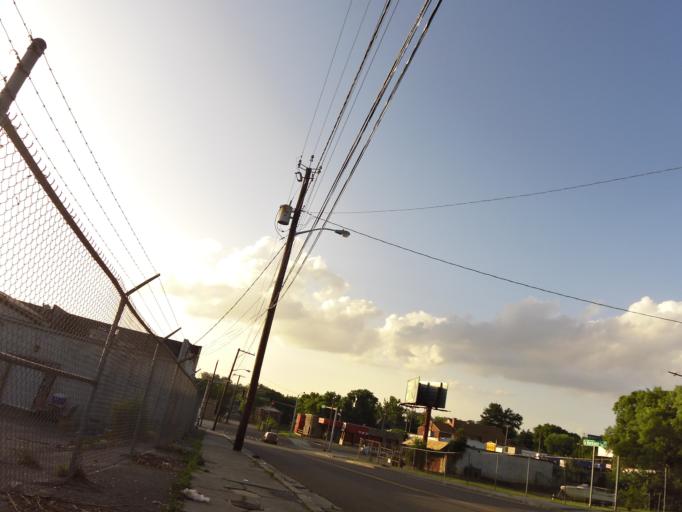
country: US
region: Tennessee
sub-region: Knox County
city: Knoxville
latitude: 35.9786
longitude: -83.9056
